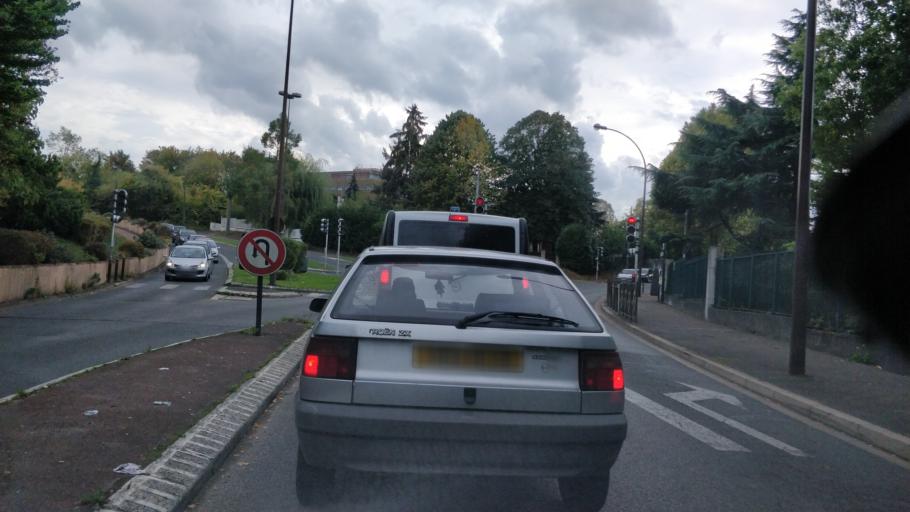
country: FR
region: Ile-de-France
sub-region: Departement de Seine-Saint-Denis
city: Livry-Gargan
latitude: 48.9186
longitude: 2.5450
